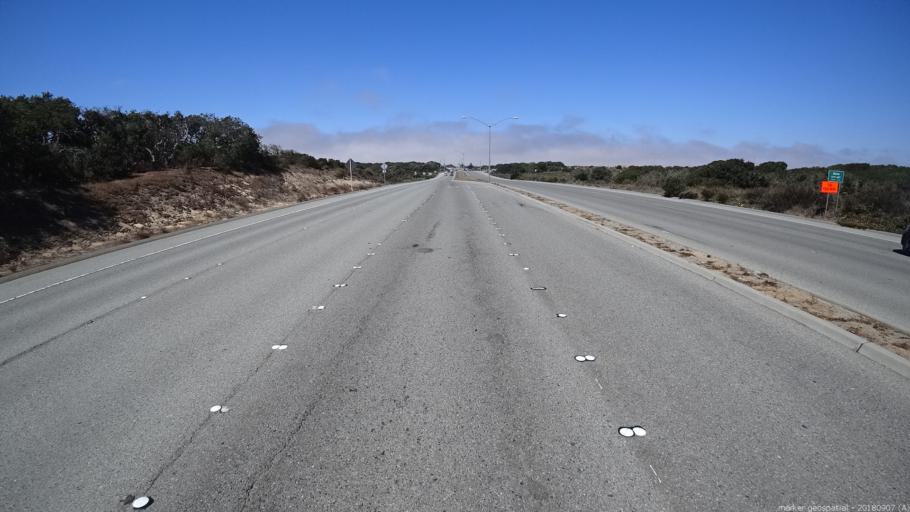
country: US
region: California
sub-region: Monterey County
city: Marina
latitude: 36.6675
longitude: -121.7581
